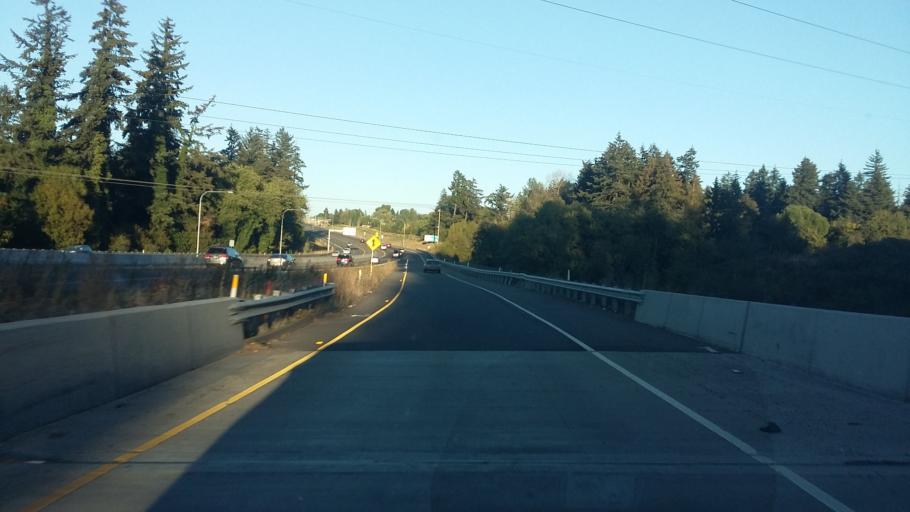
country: US
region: Washington
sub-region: Clark County
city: Minnehaha
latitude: 45.6460
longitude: -122.6395
